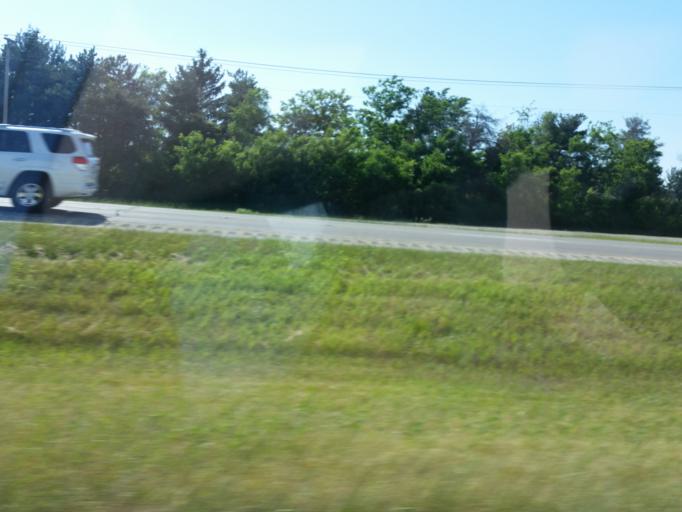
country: US
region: Illinois
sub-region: Winnebago County
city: Roscoe
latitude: 42.3968
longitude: -89.0135
